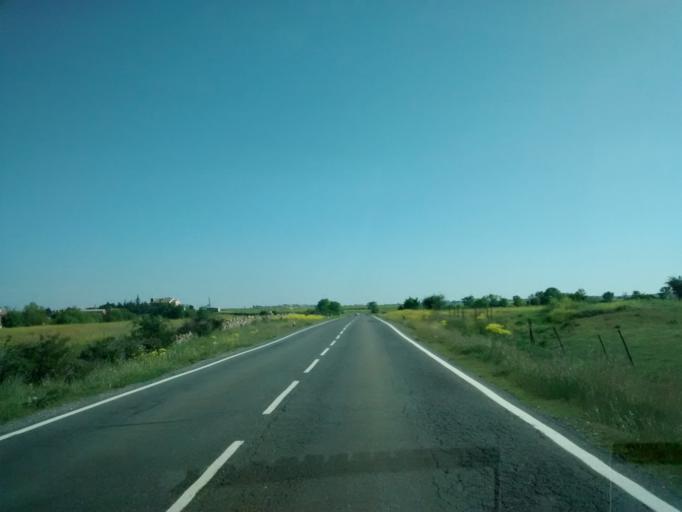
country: ES
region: Castille and Leon
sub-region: Provincia de Segovia
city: Trescasas
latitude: 40.9583
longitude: -4.0338
